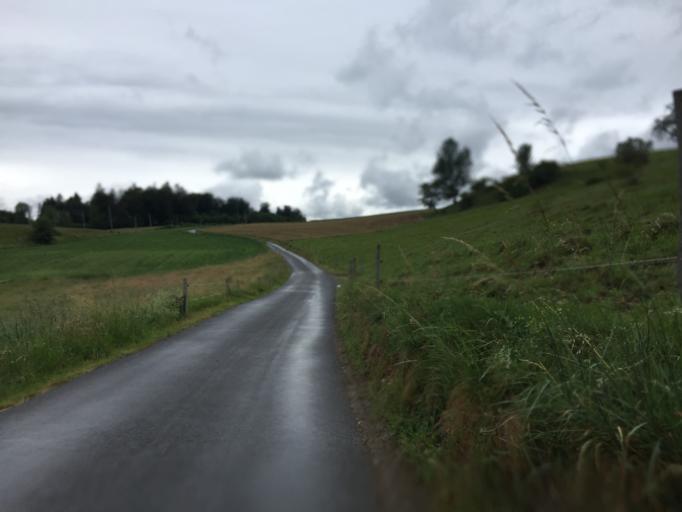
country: CH
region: Bern
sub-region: Bern-Mittelland District
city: Taegertschi
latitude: 46.8870
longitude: 7.5815
